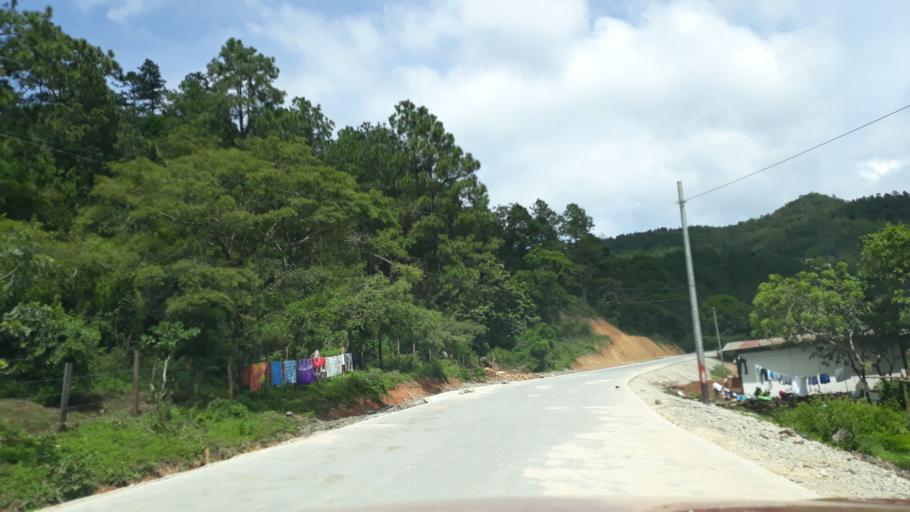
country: HN
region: El Paraiso
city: Santa Cruz
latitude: 13.7429
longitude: -86.6268
